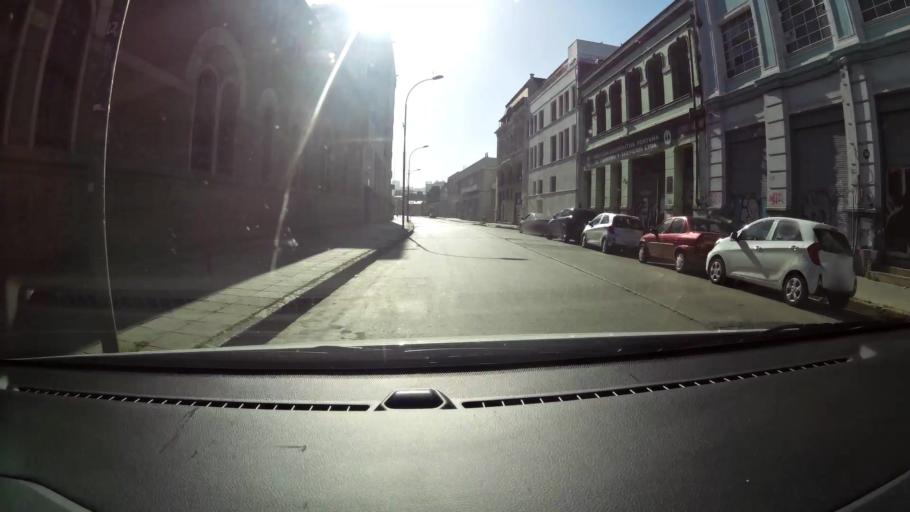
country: CL
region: Valparaiso
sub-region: Provincia de Valparaiso
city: Valparaiso
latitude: -33.0440
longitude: -71.6205
